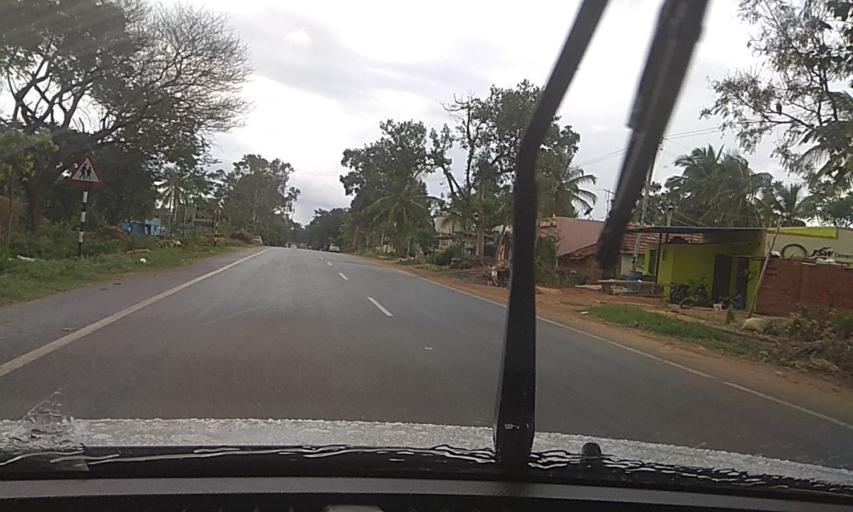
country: IN
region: Karnataka
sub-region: Tumkur
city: Kunigal
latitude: 12.9421
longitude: 77.0281
